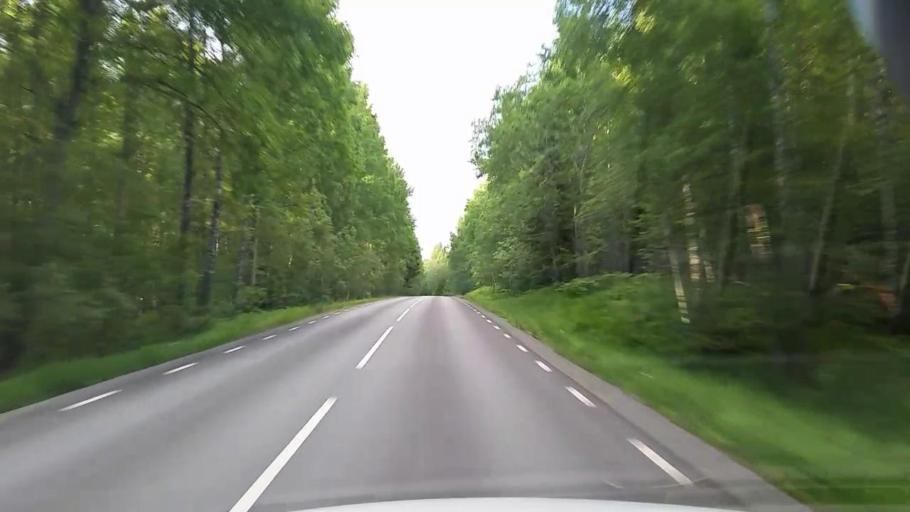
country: SE
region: Vaestmanland
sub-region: Kopings Kommun
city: Kolsva
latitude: 59.7182
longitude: 15.8307
